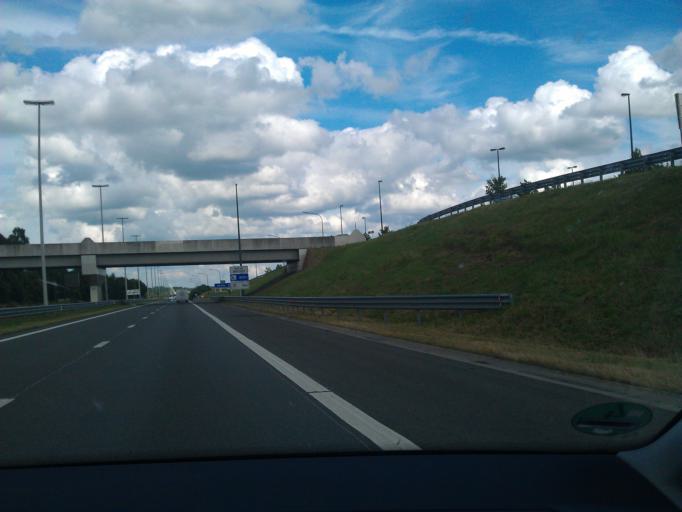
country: BE
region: Wallonia
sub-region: Province de Liege
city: Dison
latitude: 50.6443
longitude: 5.8904
